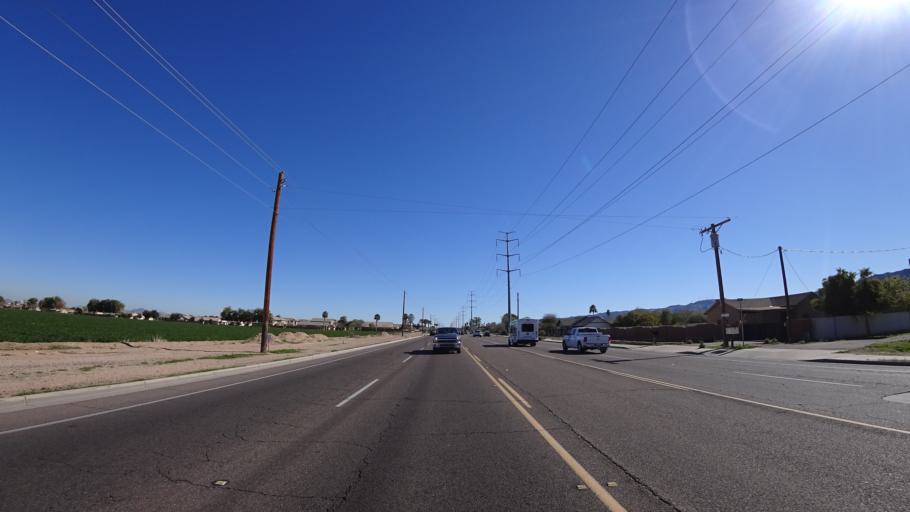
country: US
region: Arizona
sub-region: Maricopa County
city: Laveen
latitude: 33.3777
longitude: -112.1295
